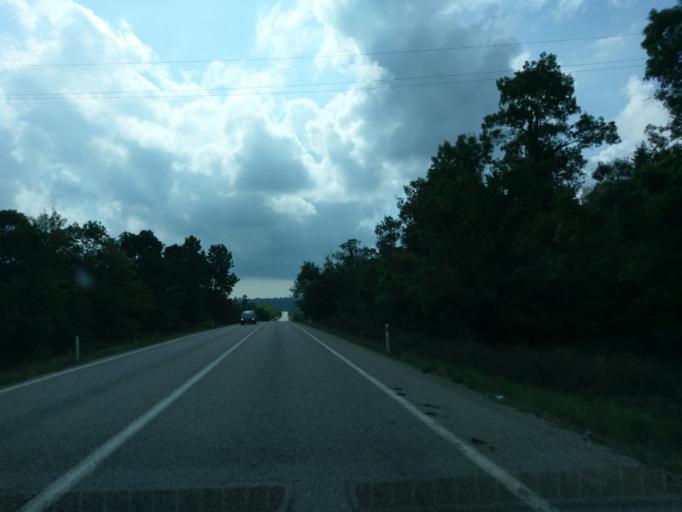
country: TR
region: Sinop
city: Sinop
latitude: 42.0208
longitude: 35.0485
